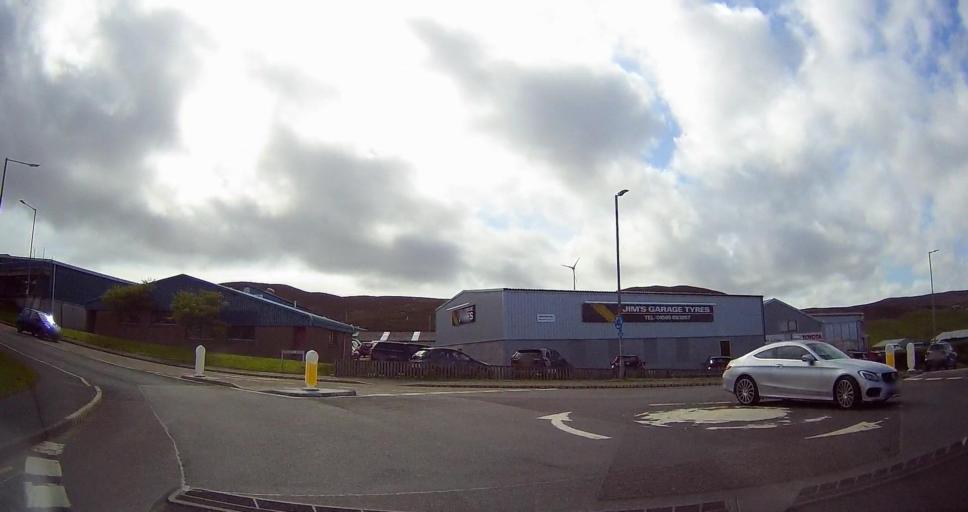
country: GB
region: Scotland
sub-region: Shetland Islands
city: Lerwick
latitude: 60.1648
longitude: -1.1647
